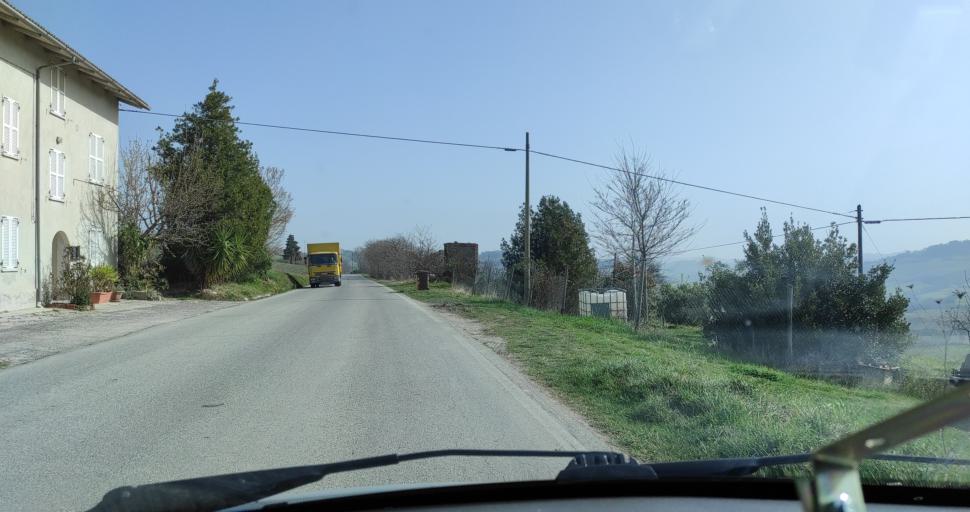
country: IT
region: The Marches
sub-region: Provincia di Macerata
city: Loro Piceno
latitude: 43.1749
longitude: 13.4335
